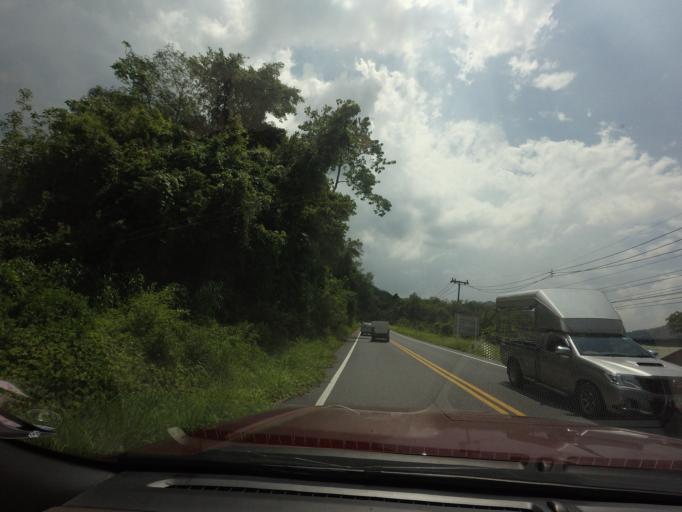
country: TH
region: Yala
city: Than To
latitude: 6.0359
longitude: 101.2118
